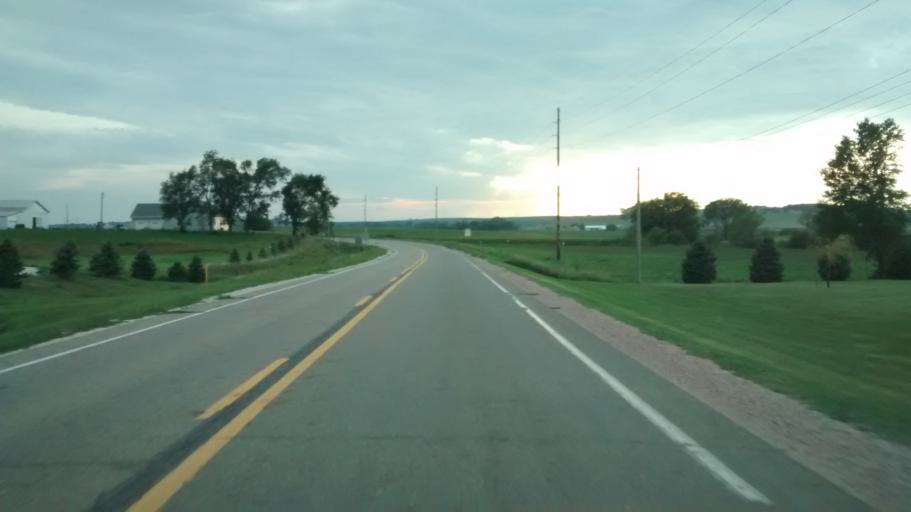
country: US
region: Iowa
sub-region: Plymouth County
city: Kingsley
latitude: 42.5830
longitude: -95.9784
